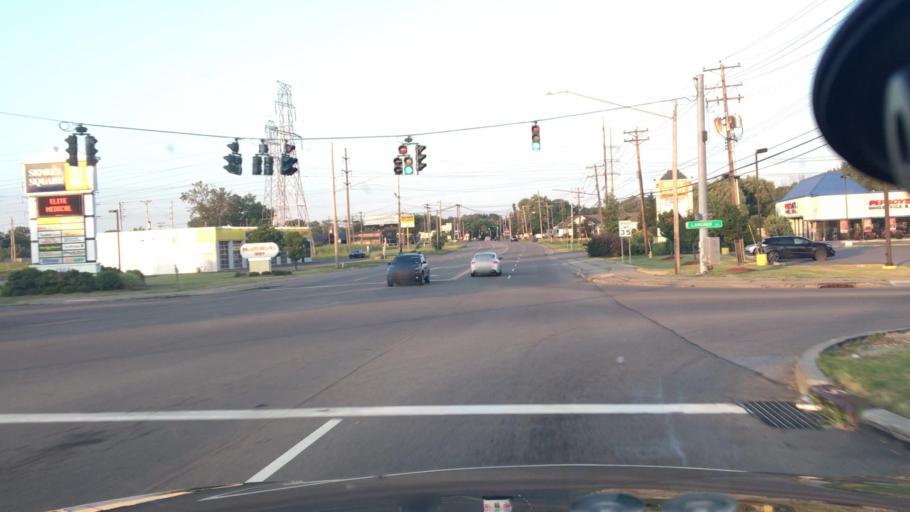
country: US
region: New York
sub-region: Erie County
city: West Seneca
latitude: 42.8287
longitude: -78.7834
